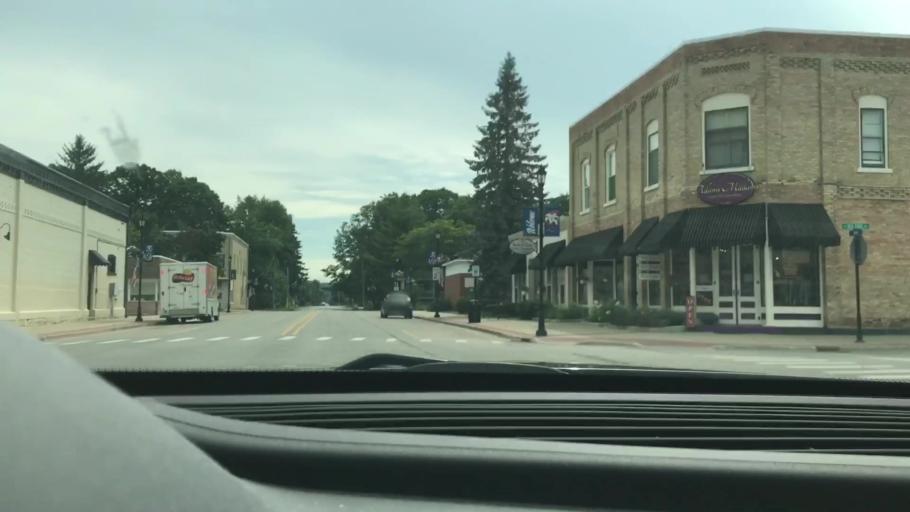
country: US
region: Michigan
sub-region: Antrim County
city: Bellaire
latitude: 45.0702
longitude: -85.2642
